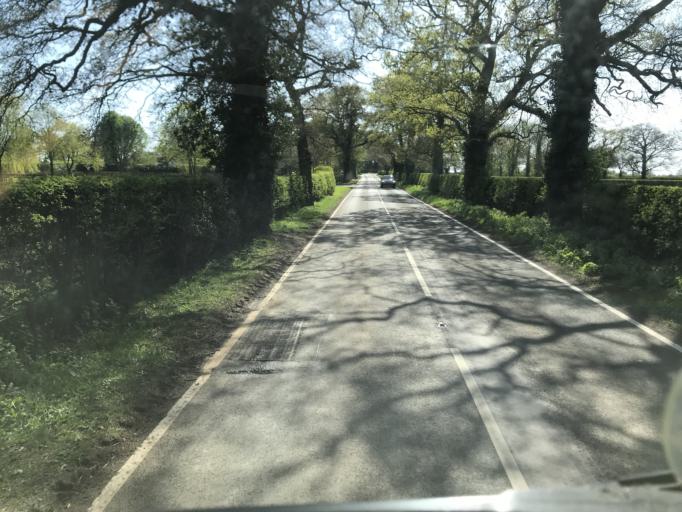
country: GB
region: England
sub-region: Cheshire East
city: Nantwich
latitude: 53.0971
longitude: -2.5128
